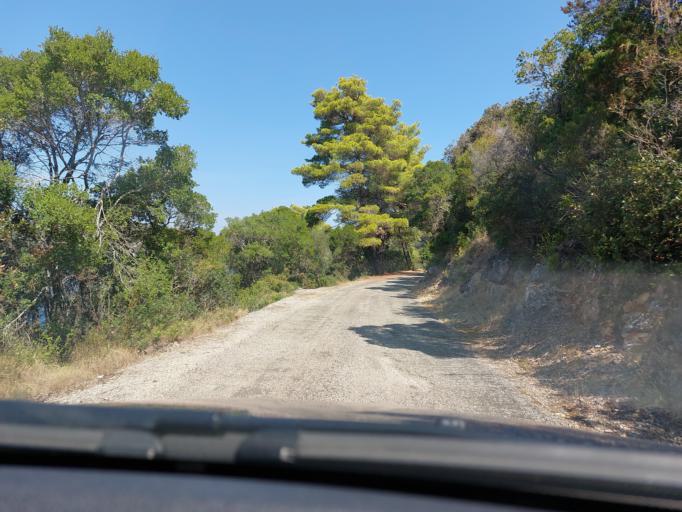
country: HR
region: Dubrovacko-Neretvanska
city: Smokvica
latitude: 42.7693
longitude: 16.8359
